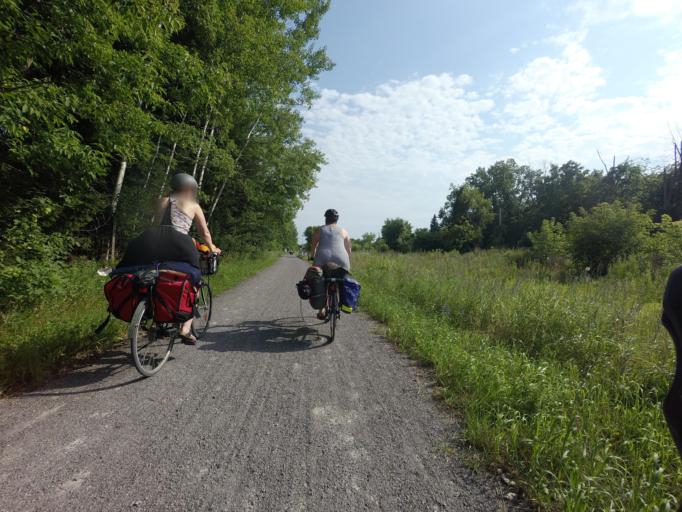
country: CA
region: Ontario
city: Prescott
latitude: 45.0222
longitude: -75.6368
